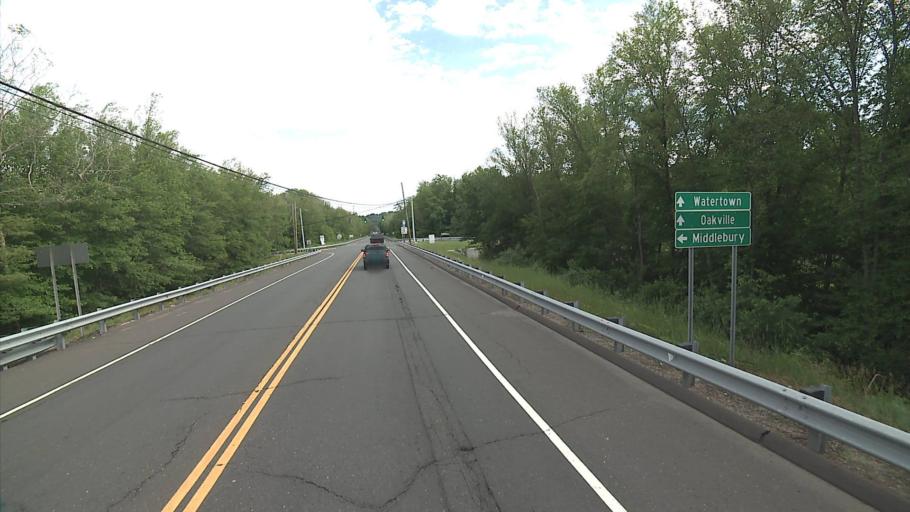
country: US
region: Connecticut
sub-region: New Haven County
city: Middlebury
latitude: 41.5224
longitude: -73.0819
